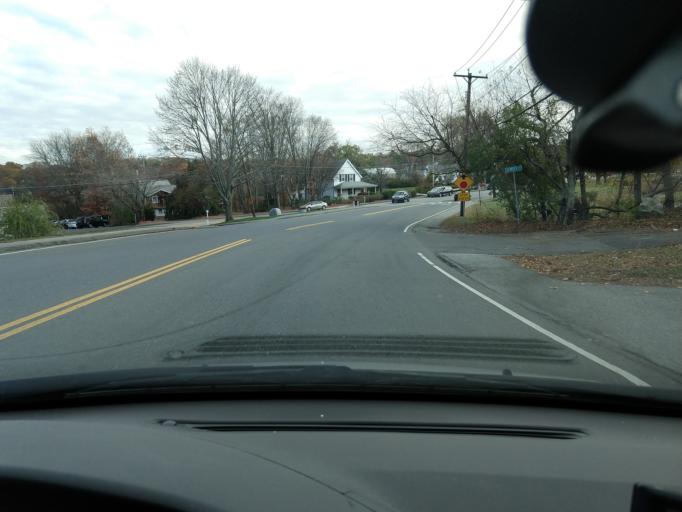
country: US
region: Massachusetts
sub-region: Middlesex County
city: Burlington
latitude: 42.5017
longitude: -71.1846
